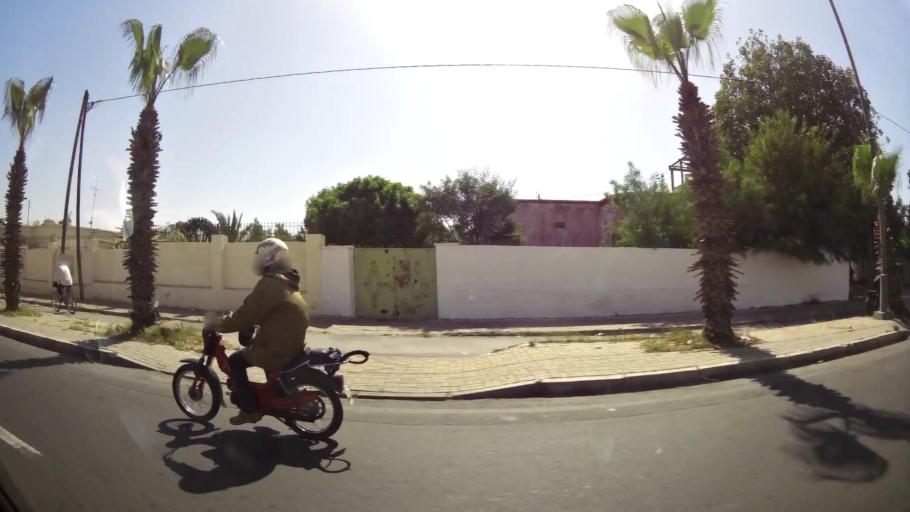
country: MA
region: Souss-Massa-Draa
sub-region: Inezgane-Ait Mellou
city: Inezgane
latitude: 30.3691
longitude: -9.5485
